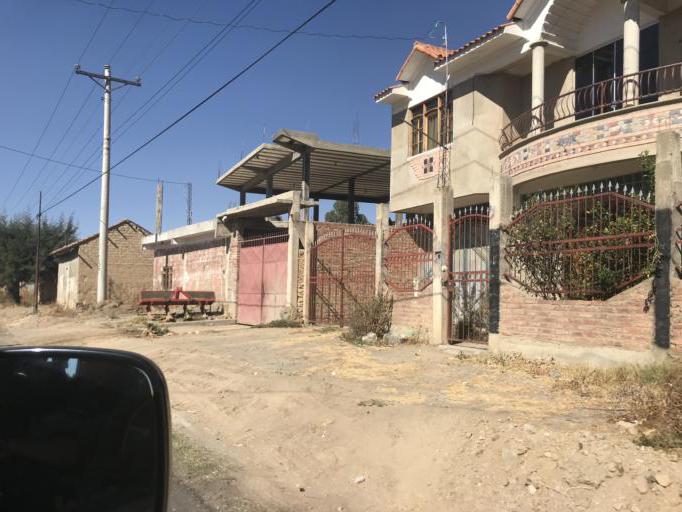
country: BO
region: Cochabamba
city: Punata
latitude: -17.5590
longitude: -65.8683
